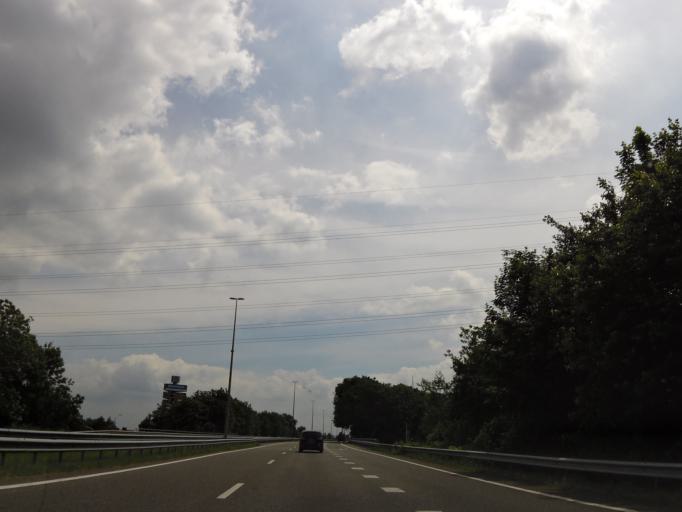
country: NL
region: Limburg
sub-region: Gemeente Simpelveld
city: Simpelveld
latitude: 50.8581
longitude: 5.9986
